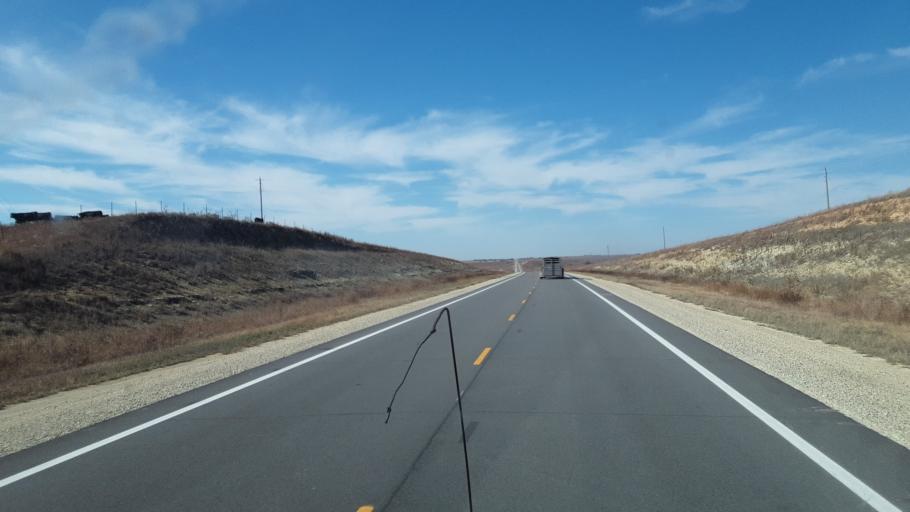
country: US
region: Kansas
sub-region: Chase County
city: Cottonwood Falls
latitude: 38.3626
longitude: -96.7365
